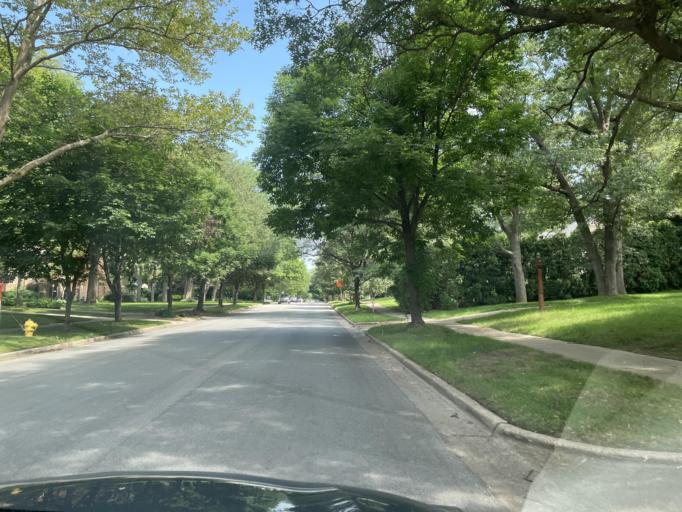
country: US
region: Michigan
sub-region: Kent County
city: East Grand Rapids
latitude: 42.9427
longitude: -85.6247
